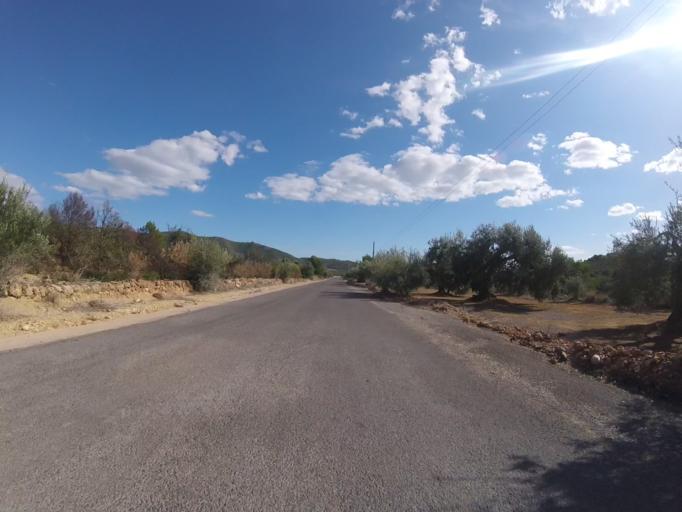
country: ES
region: Valencia
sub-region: Provincia de Castello
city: Alcala de Xivert
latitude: 40.2714
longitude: 0.2380
